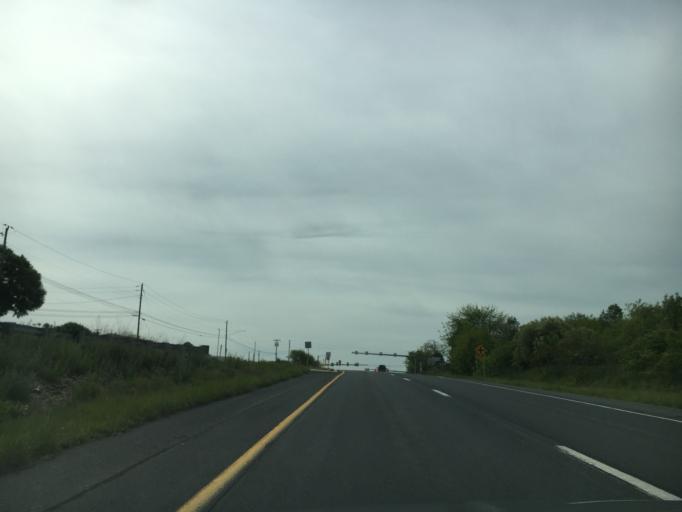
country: US
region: Pennsylvania
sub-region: Lehigh County
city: Egypt
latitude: 40.6861
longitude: -75.5229
